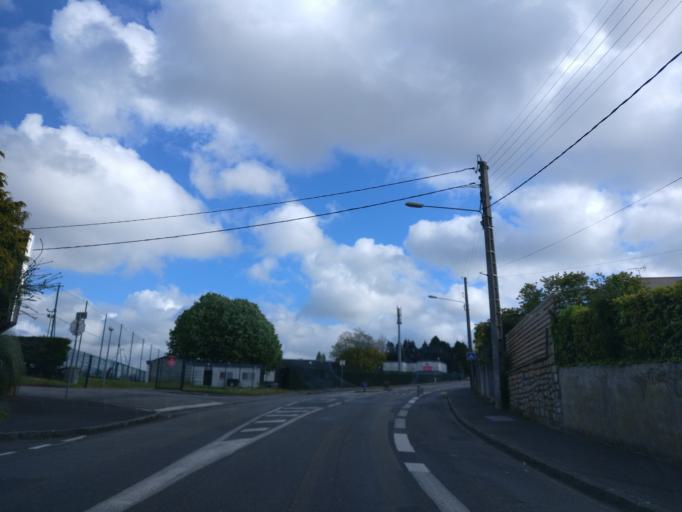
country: FR
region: Brittany
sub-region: Departement du Finistere
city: Brest
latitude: 48.4077
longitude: -4.4569
